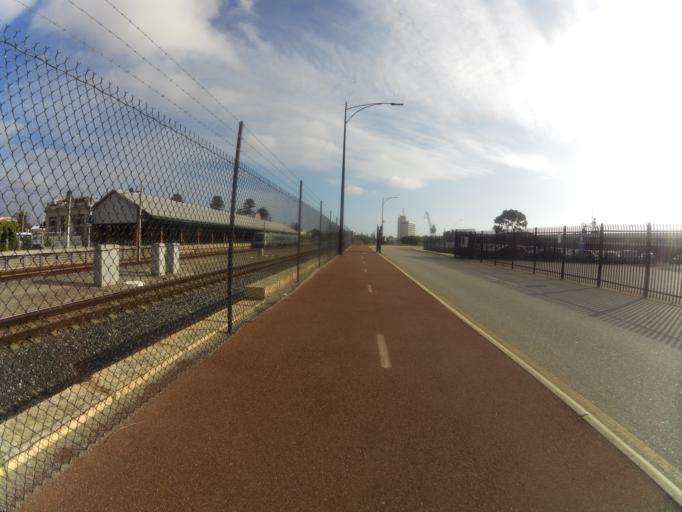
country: AU
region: Western Australia
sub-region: Fremantle
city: North Fremantle
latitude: -32.0510
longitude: 115.7458
